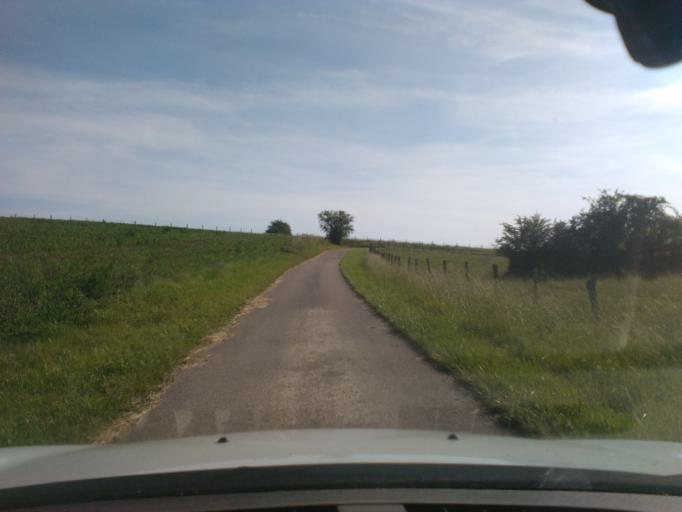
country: FR
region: Lorraine
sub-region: Departement des Vosges
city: Mirecourt
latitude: 48.2592
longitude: 6.2015
